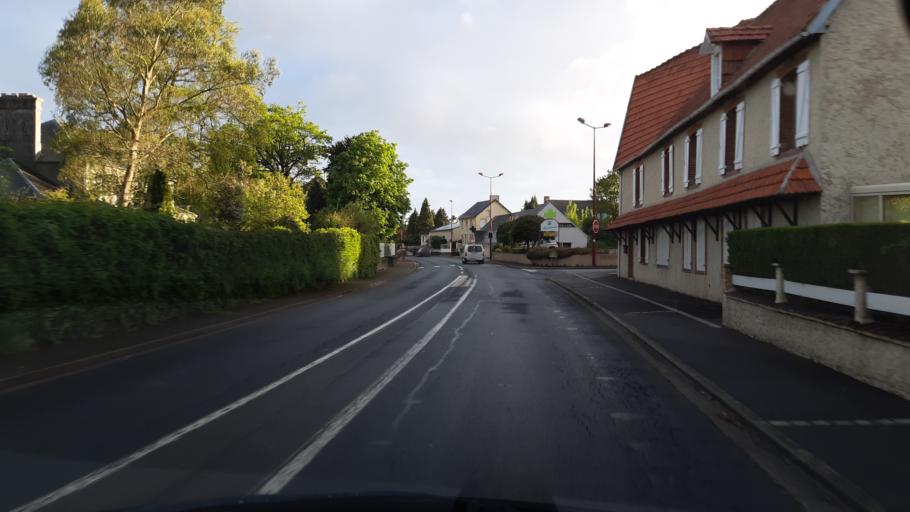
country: FR
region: Lower Normandy
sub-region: Departement de la Manche
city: Agneaux
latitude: 49.0450
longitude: -1.1281
